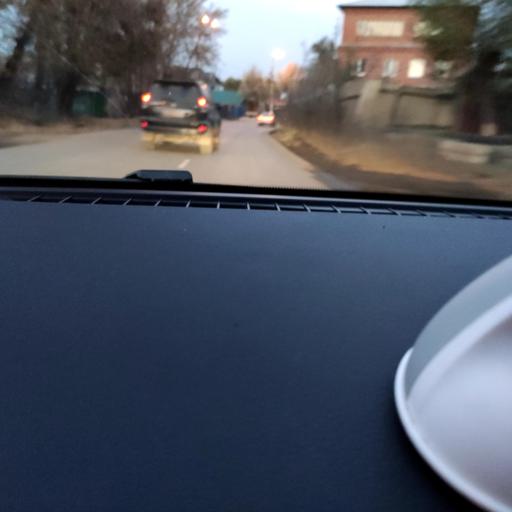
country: RU
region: Samara
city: Smyshlyayevka
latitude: 53.2350
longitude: 50.3204
